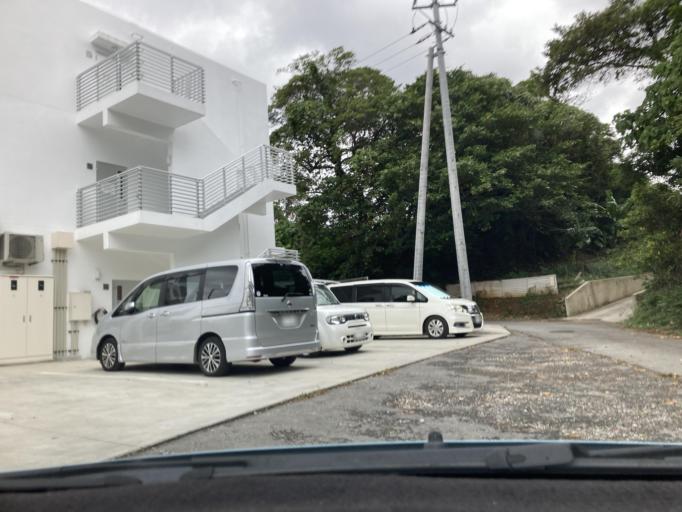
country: JP
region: Okinawa
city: Okinawa
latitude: 26.3467
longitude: 127.8066
